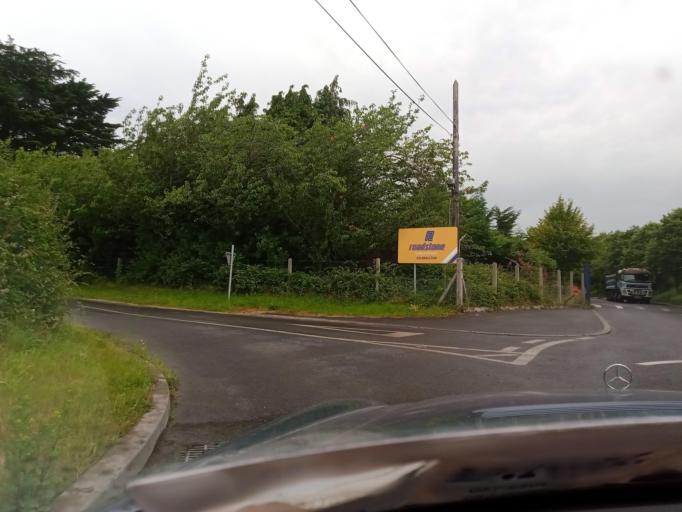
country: IE
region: Leinster
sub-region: Kilkenny
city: Mooncoin
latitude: 52.2842
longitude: -7.1881
